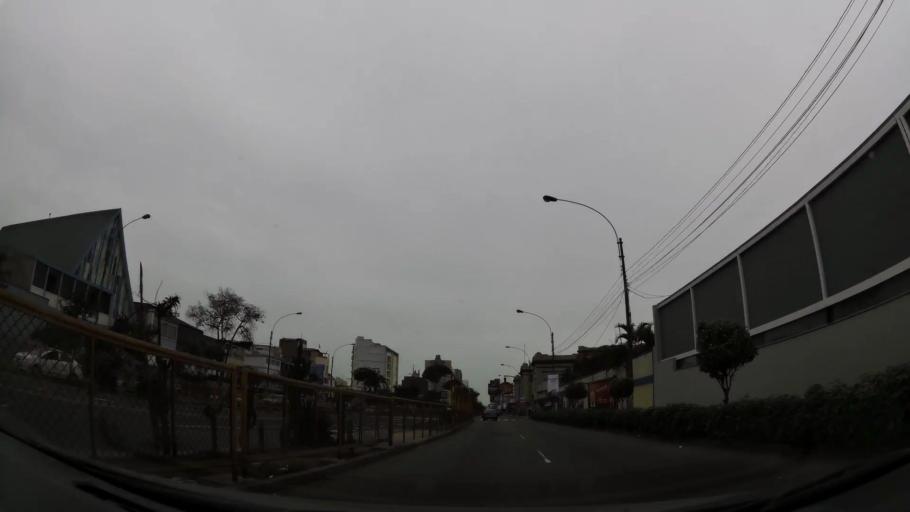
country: PE
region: Lima
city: Lima
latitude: -12.0623
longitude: -77.0434
